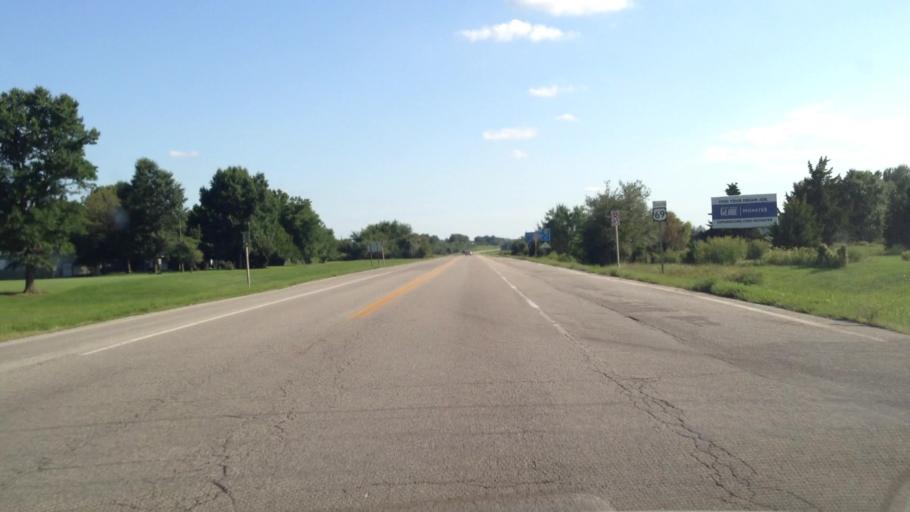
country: US
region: Kansas
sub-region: Crawford County
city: Arma
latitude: 37.5428
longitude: -94.7102
